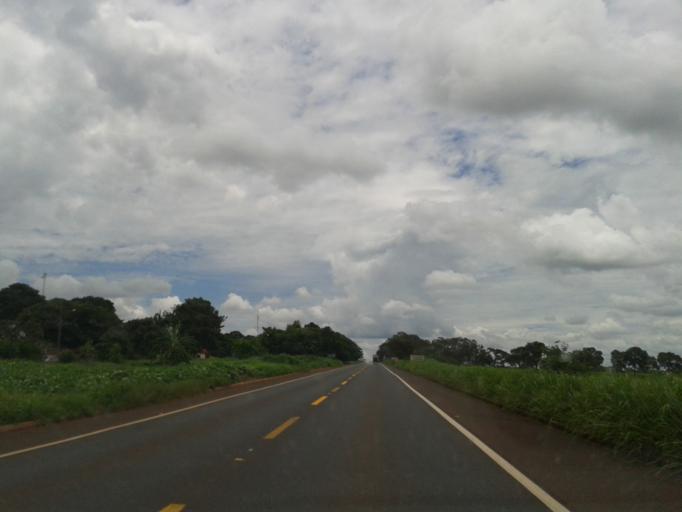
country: BR
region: Minas Gerais
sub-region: Santa Vitoria
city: Santa Vitoria
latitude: -18.9326
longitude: -49.8345
